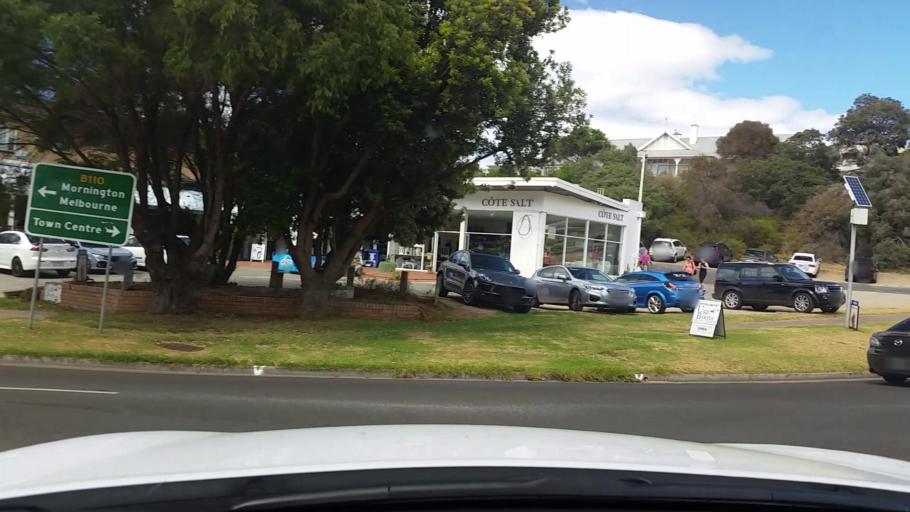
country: AU
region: Victoria
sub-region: Mornington Peninsula
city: Sorrento
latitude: -38.3384
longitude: 144.7438
